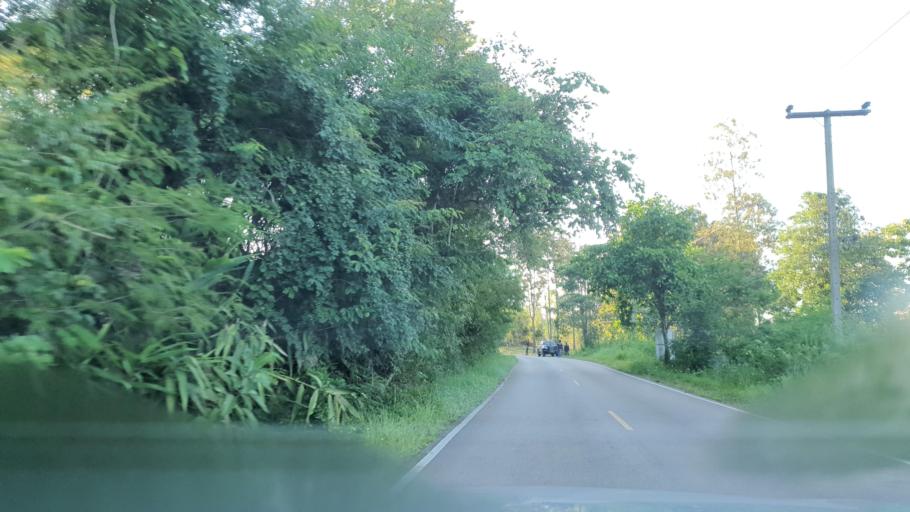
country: TH
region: Chiang Mai
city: Mae On
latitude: 18.8438
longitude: 99.2796
